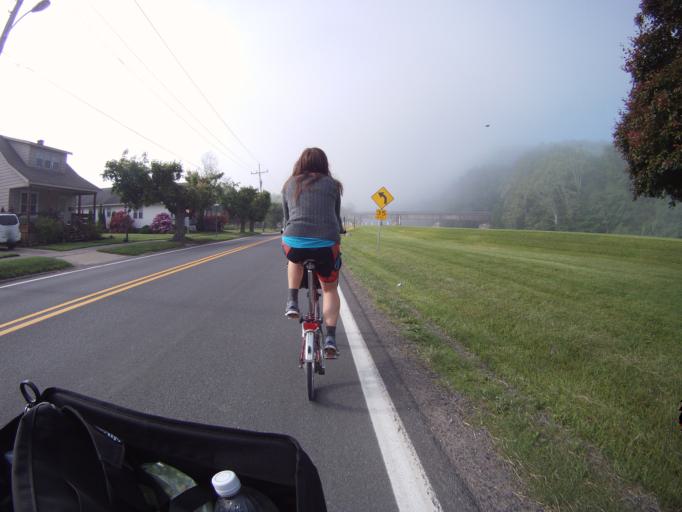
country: US
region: Pennsylvania
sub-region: Somerset County
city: Milford
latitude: 39.8057
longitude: -79.3567
